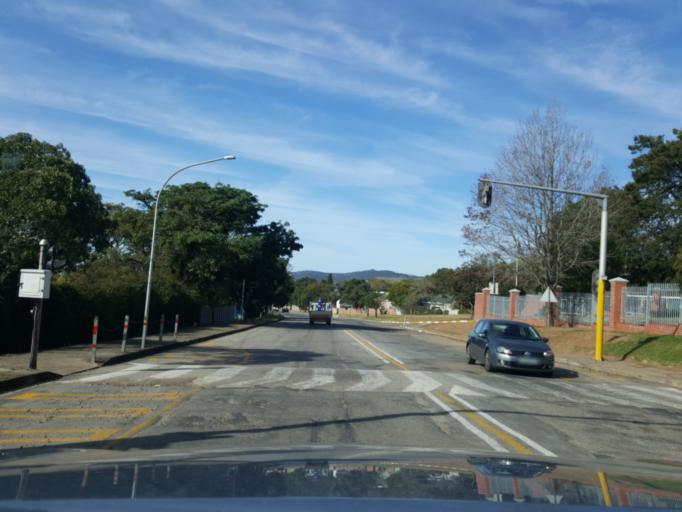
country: ZA
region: Eastern Cape
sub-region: Cacadu District Municipality
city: Grahamstown
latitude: -33.3063
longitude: 26.5124
